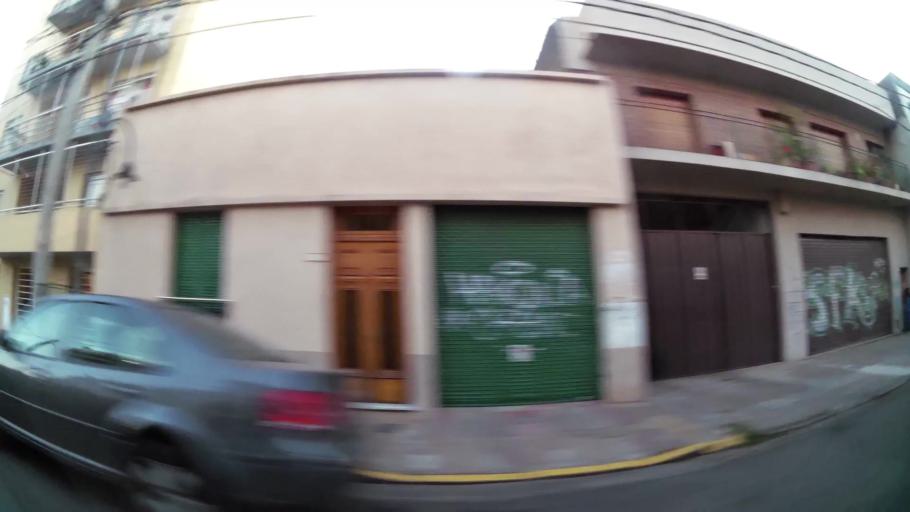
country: AR
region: Buenos Aires
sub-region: Partido de Tigre
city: Tigre
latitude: -34.4371
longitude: -58.5633
